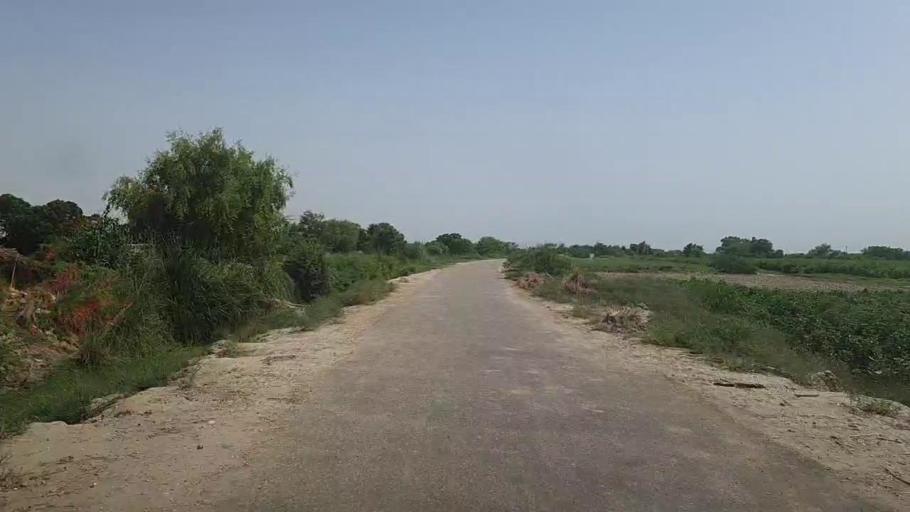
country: PK
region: Sindh
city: Pad Idan
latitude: 26.8031
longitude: 68.3325
